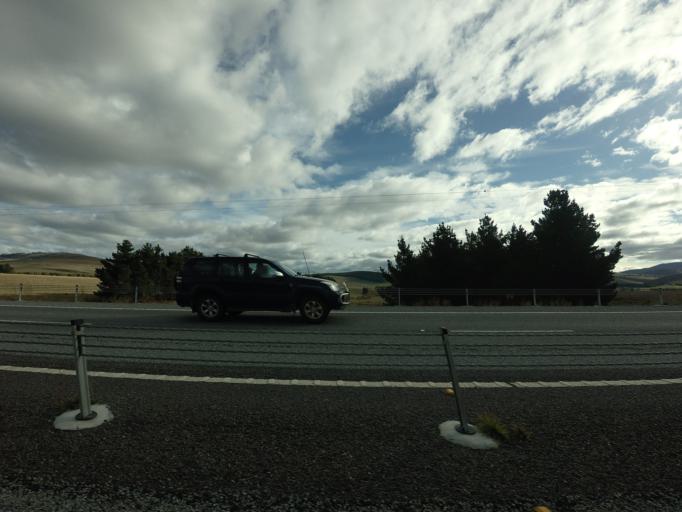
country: AU
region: Tasmania
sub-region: Brighton
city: Bridgewater
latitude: -42.4992
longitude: 147.1866
